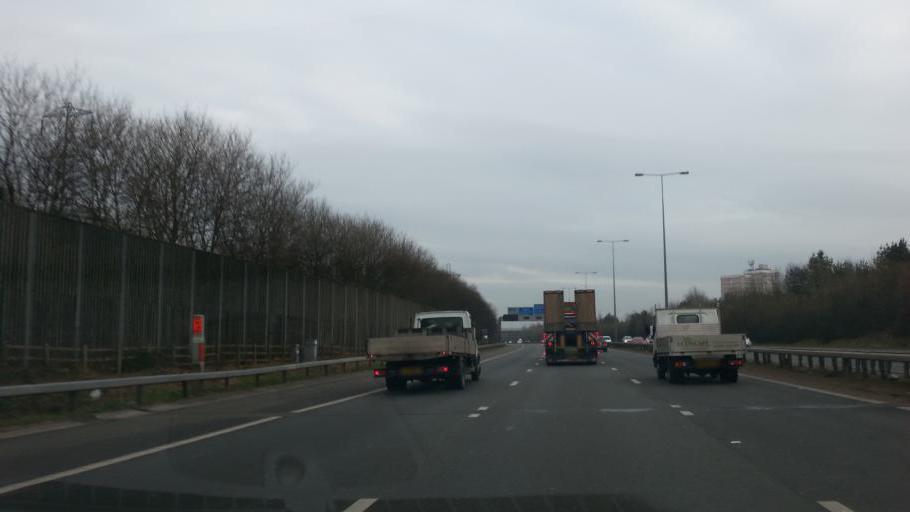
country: GB
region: England
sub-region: Borough of Rochdale
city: Middleton
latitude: 53.5302
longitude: -2.1897
